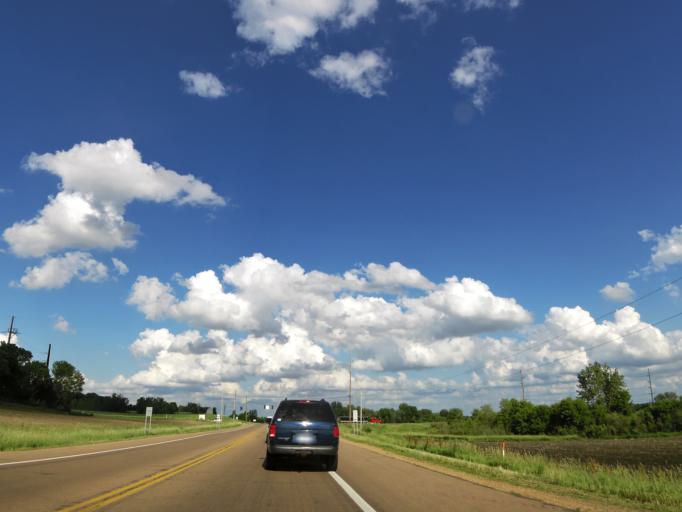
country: US
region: Minnesota
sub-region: Carver County
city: Victoria
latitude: 44.8079
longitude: -93.6549
